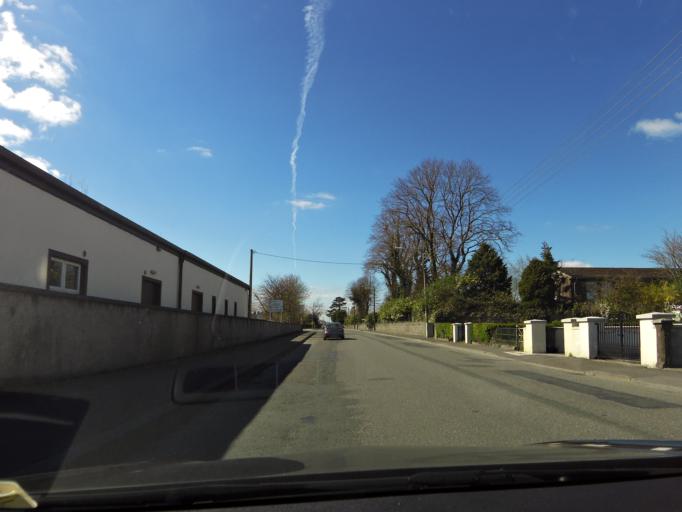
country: IE
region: Leinster
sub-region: Kildare
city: Athy
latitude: 52.9970
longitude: -6.9945
